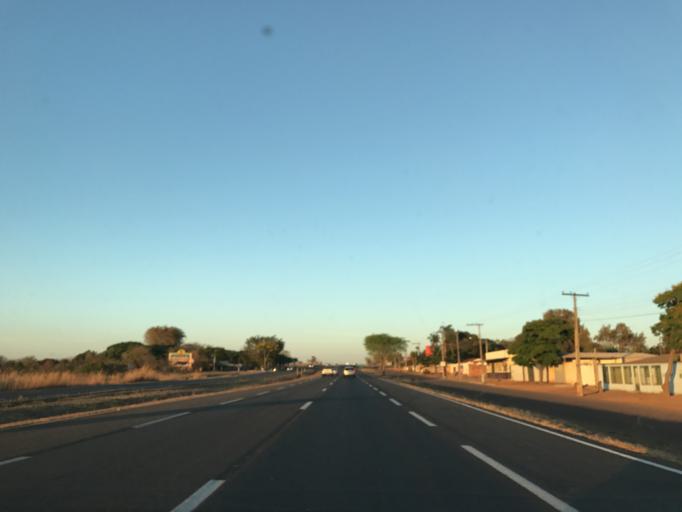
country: BR
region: Goias
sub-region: Abadiania
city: Abadiania
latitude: -16.1889
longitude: -48.7225
